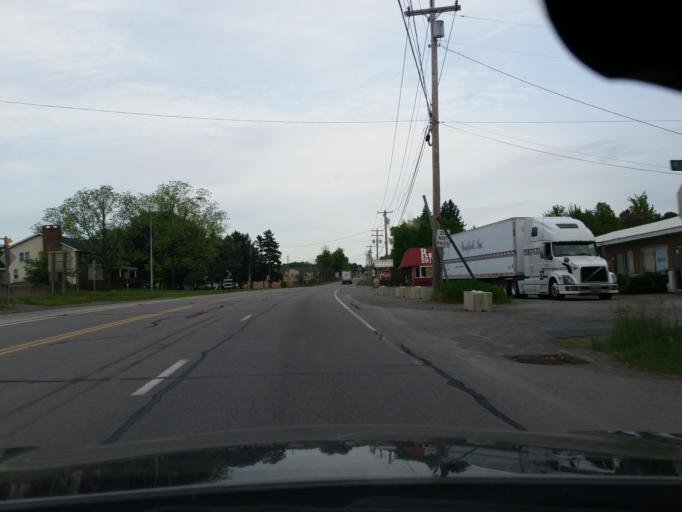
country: US
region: Pennsylvania
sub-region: Elk County
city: Ridgway
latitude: 41.4091
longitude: -78.7091
